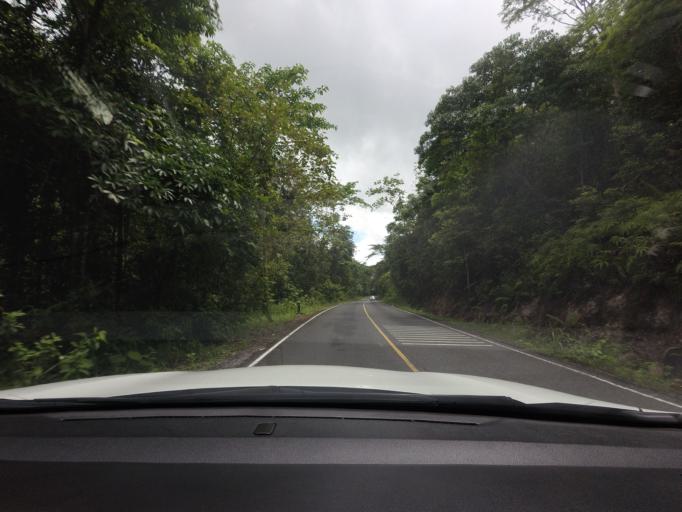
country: TH
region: Nakhon Nayok
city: Nakhon Nayok
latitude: 14.3545
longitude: 101.3429
